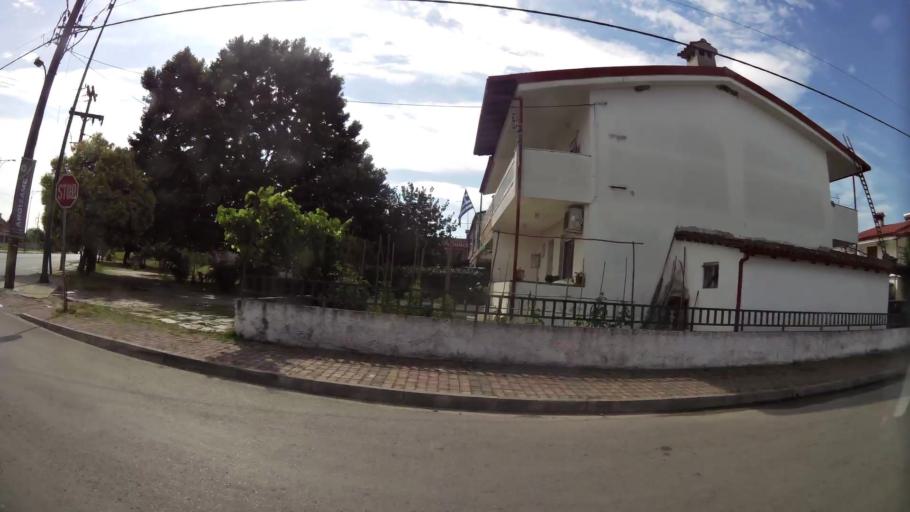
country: GR
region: Central Macedonia
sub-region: Nomos Pierias
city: Katerini
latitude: 40.2839
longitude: 22.5155
